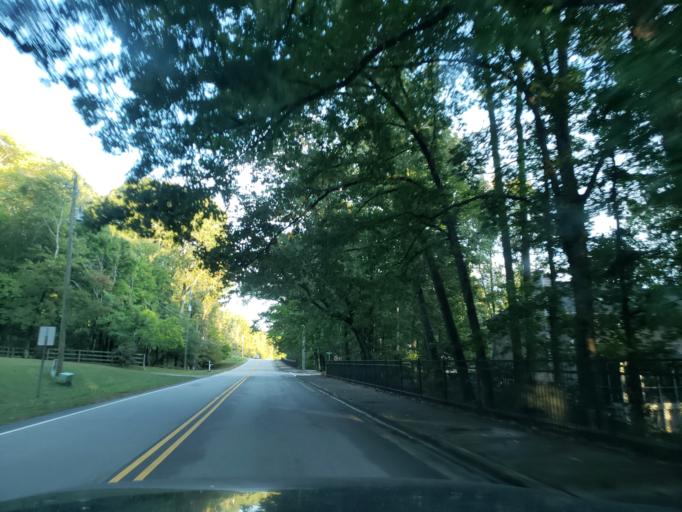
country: US
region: North Carolina
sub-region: Wake County
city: Apex
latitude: 35.7416
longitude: -78.8201
